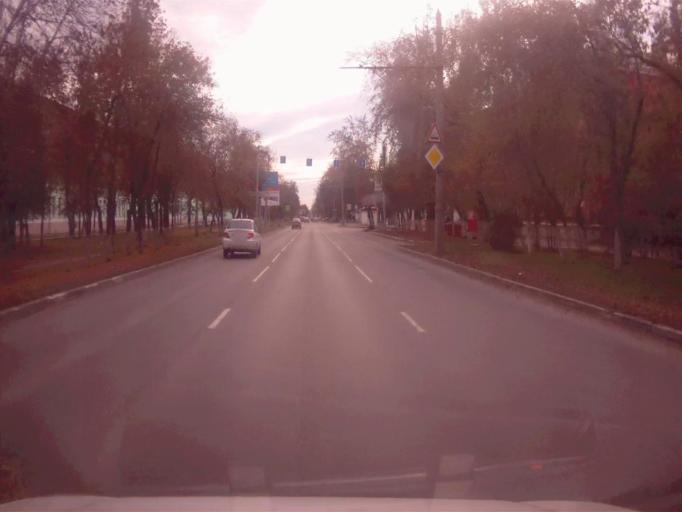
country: RU
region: Chelyabinsk
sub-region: Gorod Chelyabinsk
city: Chelyabinsk
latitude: 55.1220
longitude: 61.4732
